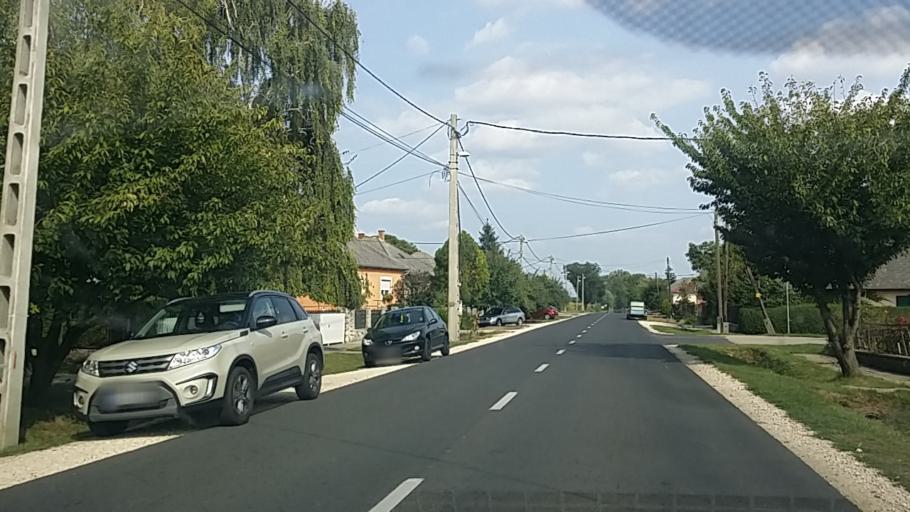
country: HU
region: Komarom-Esztergom
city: Babolna
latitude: 47.6494
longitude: 17.9306
